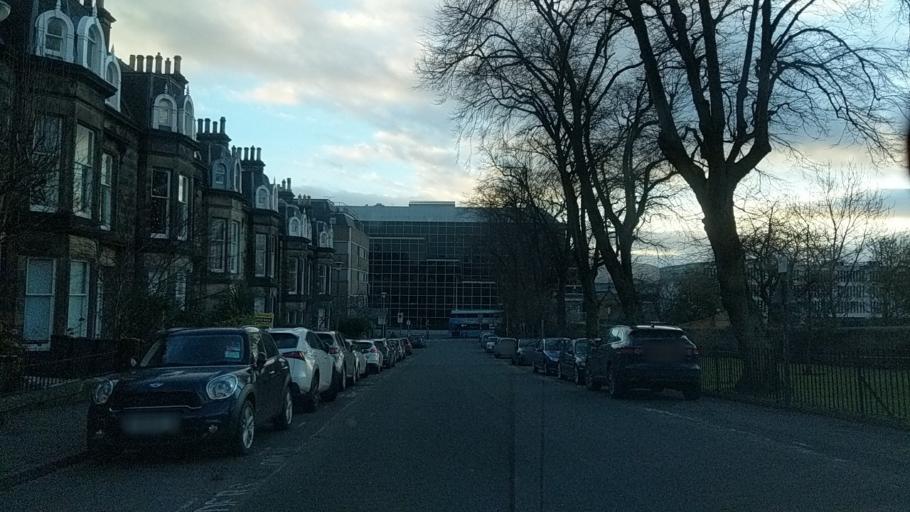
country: GB
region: Scotland
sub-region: Edinburgh
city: Edinburgh
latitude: 55.9470
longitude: -3.2235
